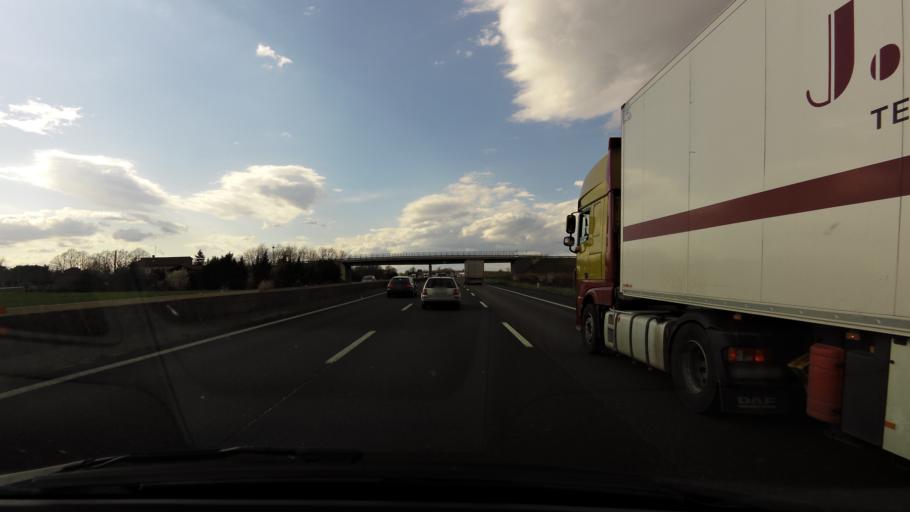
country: IT
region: Emilia-Romagna
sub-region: Provincia di Bologna
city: Imola
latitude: 44.3895
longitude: 11.7176
